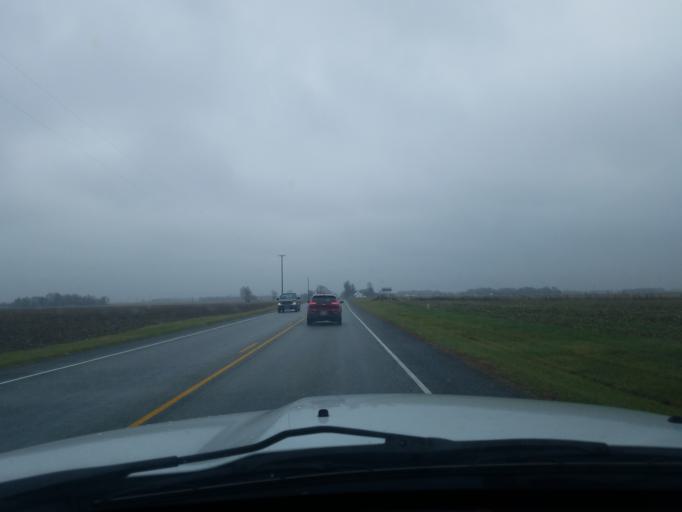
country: US
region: Indiana
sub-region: Howard County
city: Indian Heights
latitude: 40.4196
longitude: -86.0668
